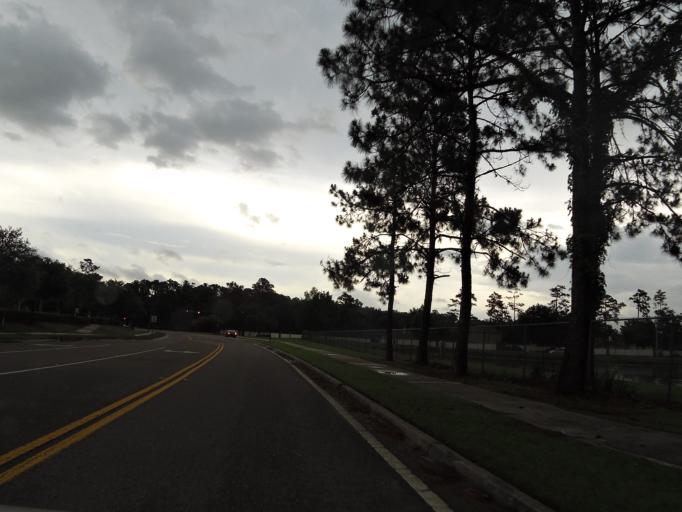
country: US
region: Florida
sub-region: Nassau County
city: Yulee
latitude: 30.4839
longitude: -81.6056
